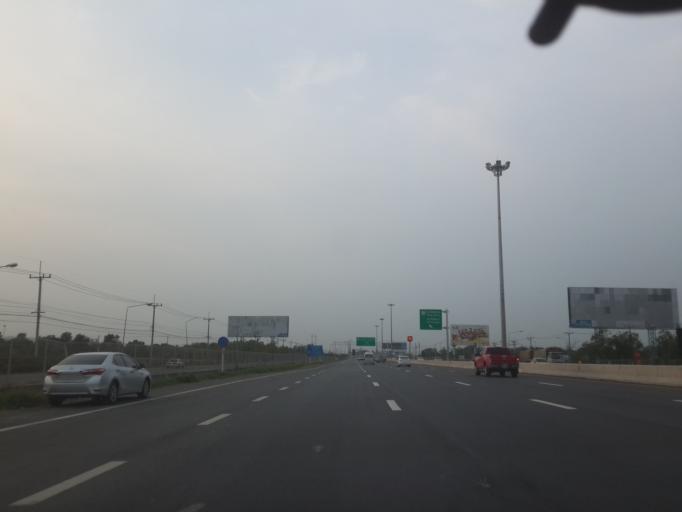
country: TH
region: Chachoengsao
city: Bang Pakong
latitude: 13.5432
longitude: 101.0054
